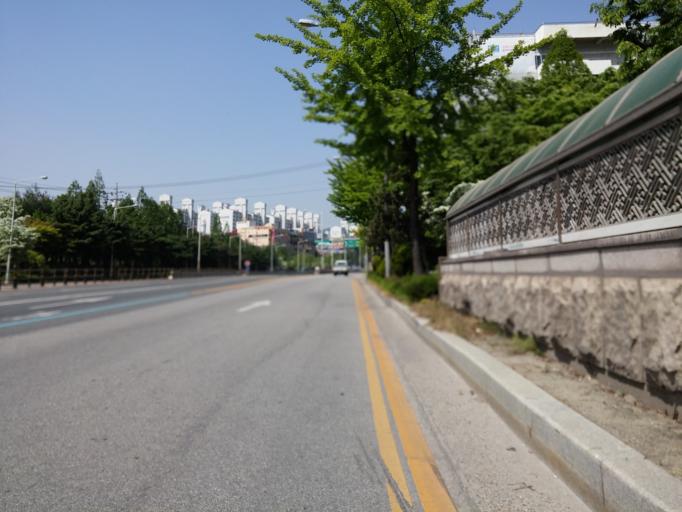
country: KR
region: Daejeon
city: Daejeon
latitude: 36.3022
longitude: 127.3388
